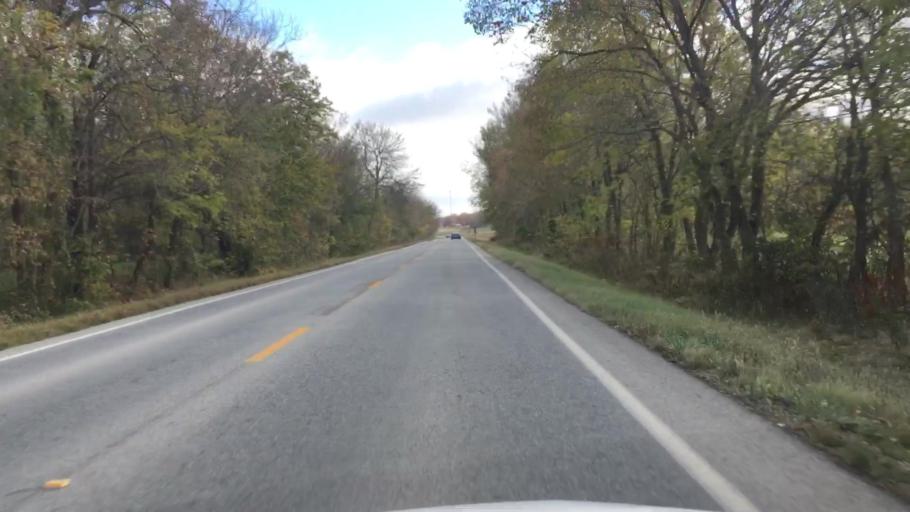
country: US
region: Arkansas
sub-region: Benton County
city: Gentry
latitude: 36.2591
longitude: -94.4105
